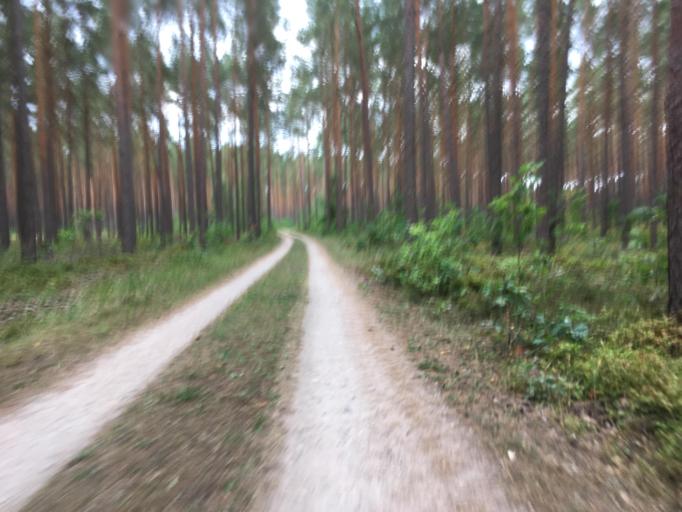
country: DE
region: Brandenburg
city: Lychen
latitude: 53.1243
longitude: 13.2419
